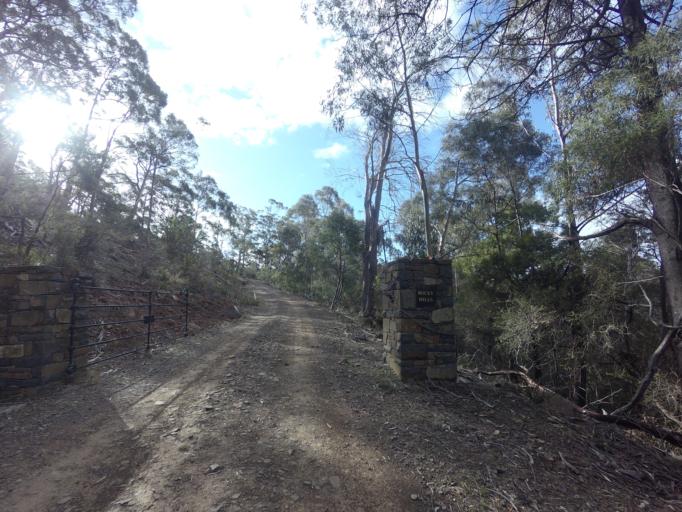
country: AU
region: Tasmania
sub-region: Sorell
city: Sorell
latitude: -42.2289
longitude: 148.0040
